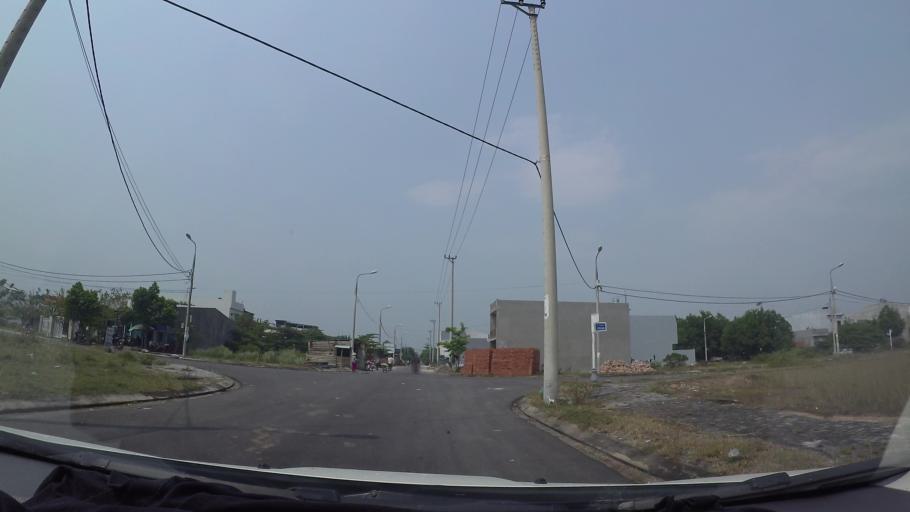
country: VN
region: Da Nang
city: Cam Le
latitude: 15.9798
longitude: 108.2162
